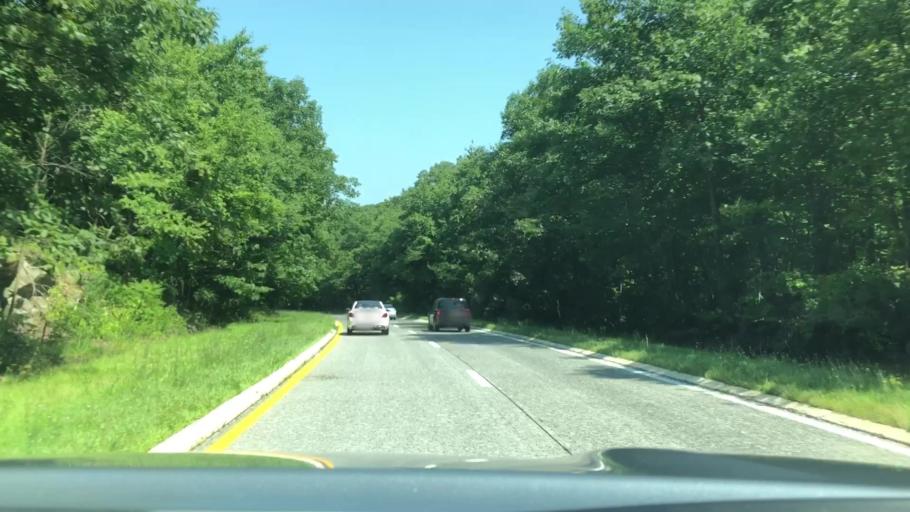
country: US
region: New York
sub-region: Rockland County
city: Stony Point
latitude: 41.2701
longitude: -74.0306
